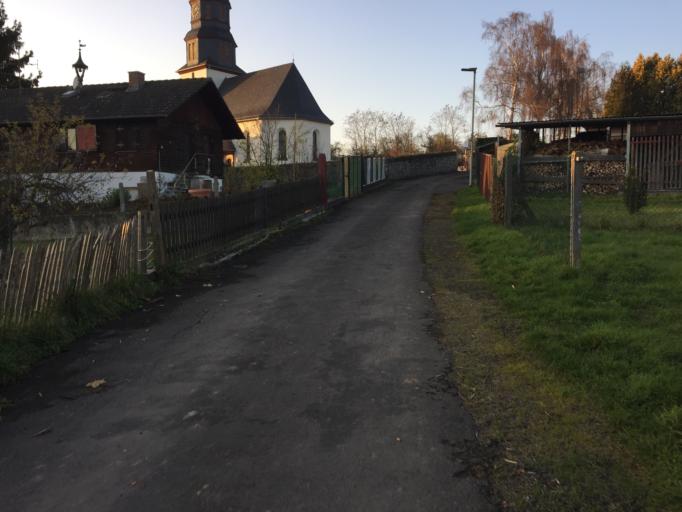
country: DE
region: Hesse
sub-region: Regierungsbezirk Darmstadt
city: Munzenberg
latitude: 50.4818
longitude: 8.7589
